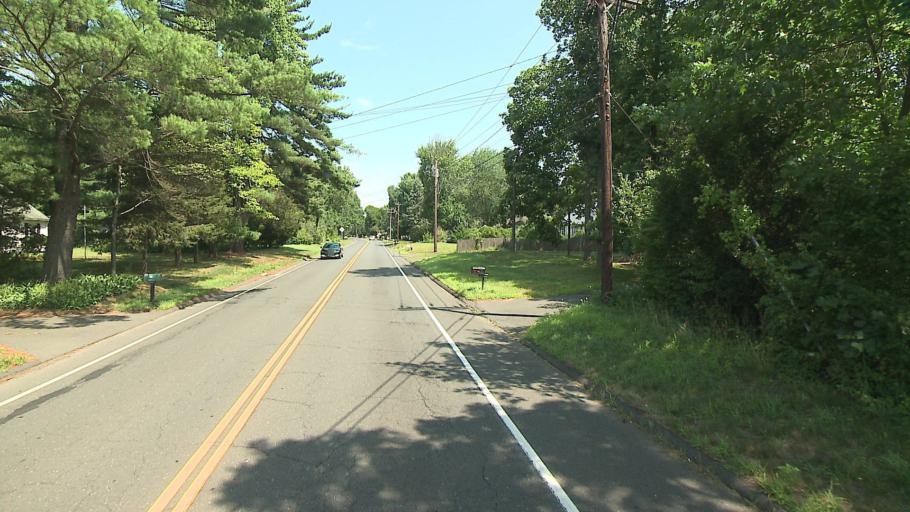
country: US
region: Connecticut
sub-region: Hartford County
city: Plainville
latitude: 41.6979
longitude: -72.8778
